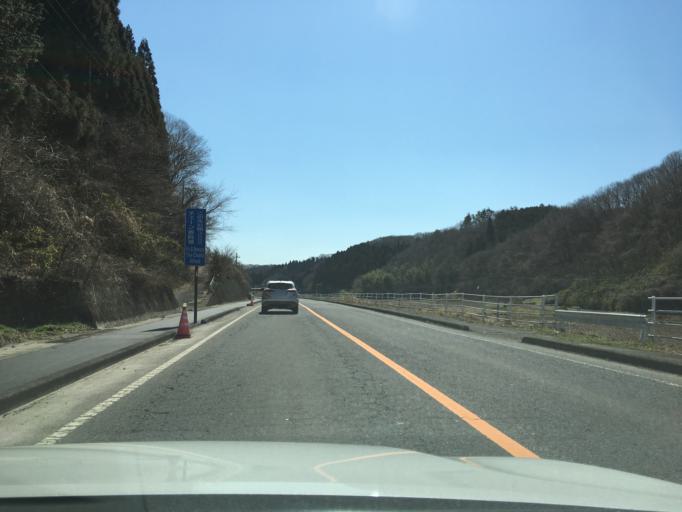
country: JP
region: Tochigi
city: Kuroiso
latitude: 37.0456
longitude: 140.1702
